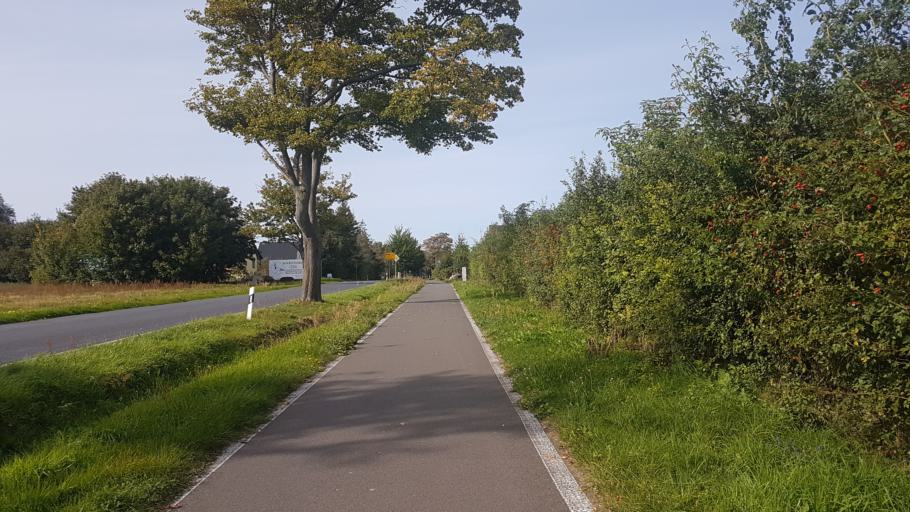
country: DE
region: Mecklenburg-Vorpommern
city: Gingst
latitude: 54.4514
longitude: 13.1828
